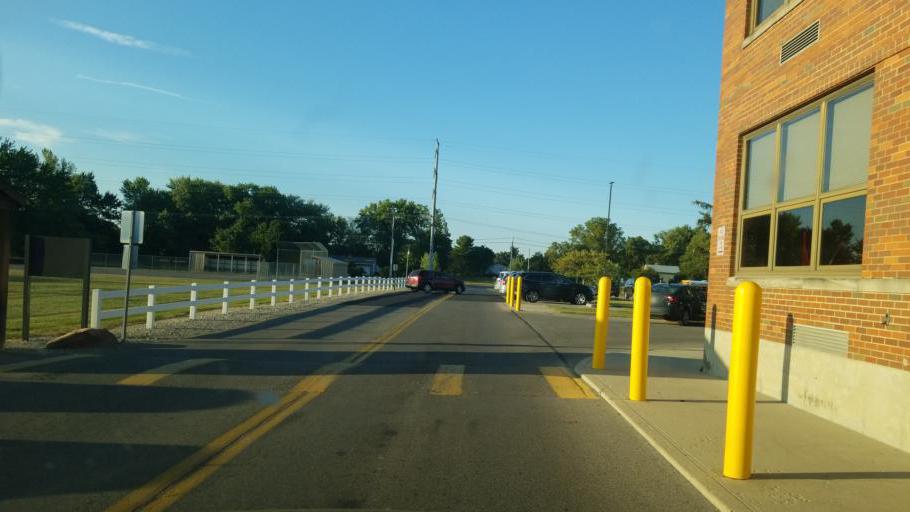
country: US
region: Ohio
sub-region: Delaware County
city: Lewis Center
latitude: 40.2123
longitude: -83.0234
